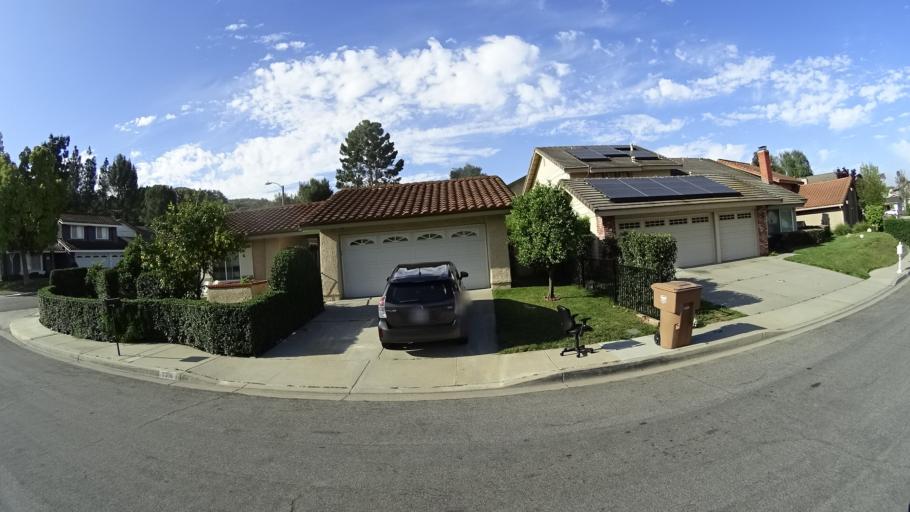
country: US
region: California
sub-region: Ventura County
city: Casa Conejo
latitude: 34.1735
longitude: -118.9465
